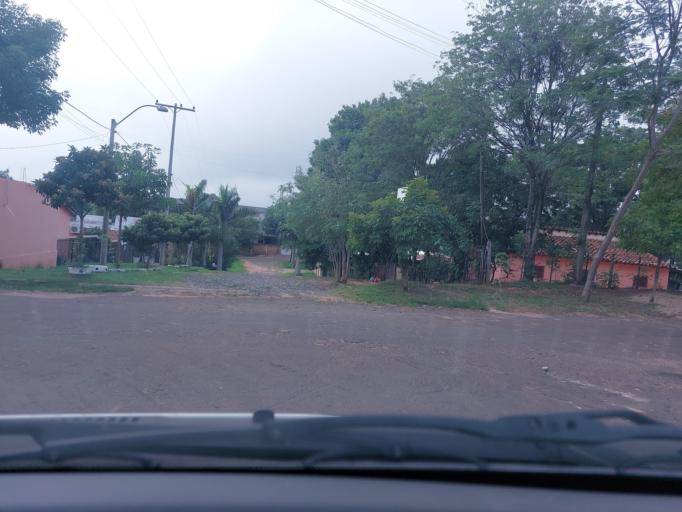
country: PY
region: San Pedro
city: Guayaybi
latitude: -24.6641
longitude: -56.4408
